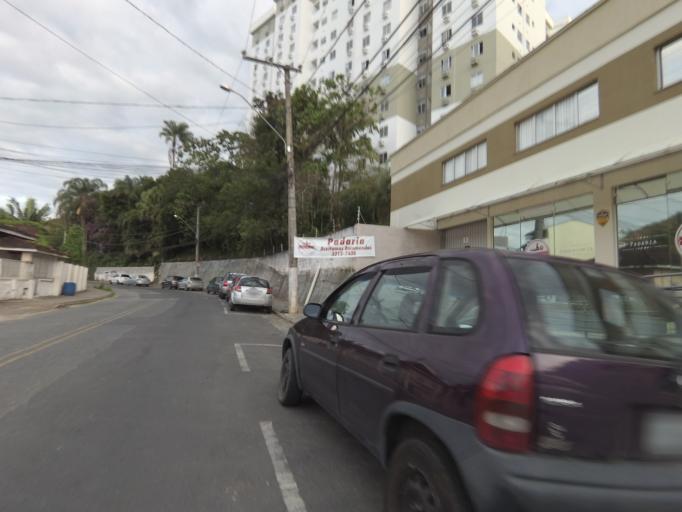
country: BR
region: Santa Catarina
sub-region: Blumenau
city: Blumenau
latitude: -26.9274
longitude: -49.0507
